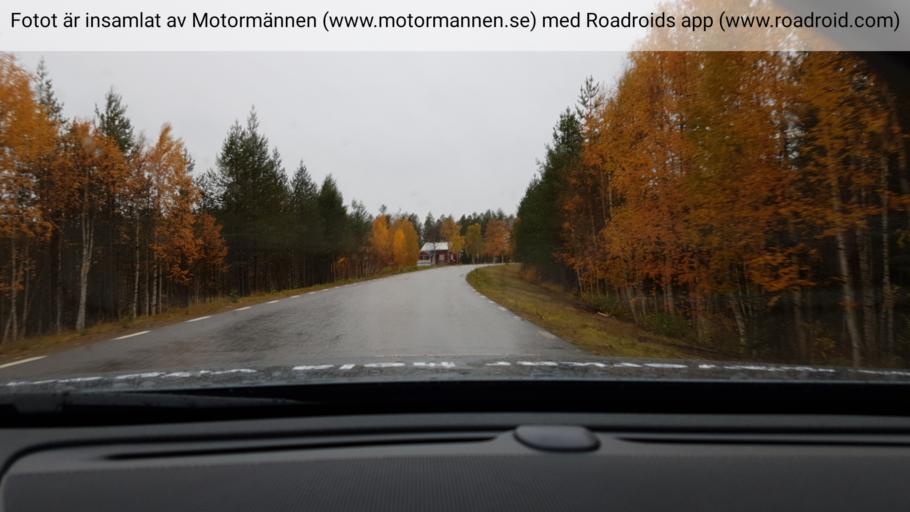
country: SE
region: Norrbotten
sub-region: Pajala Kommun
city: Pajala
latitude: 66.9237
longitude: 23.0150
